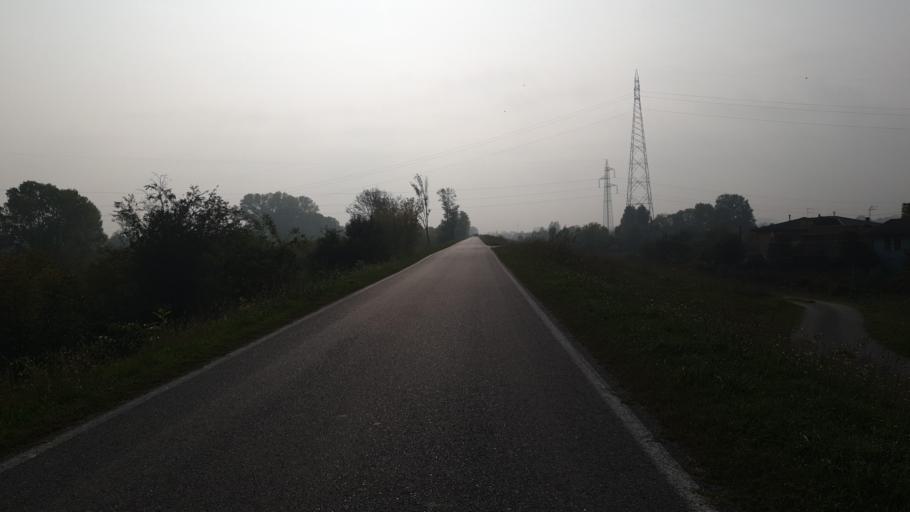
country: IT
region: Veneto
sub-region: Provincia di Venezia
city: Galta
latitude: 45.3839
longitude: 12.0173
